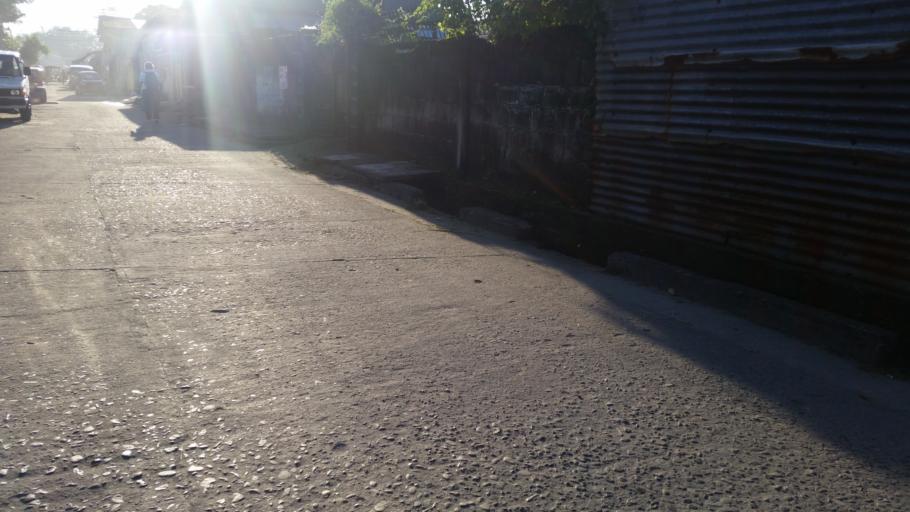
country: PH
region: Central Luzon
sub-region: Province of Pampanga
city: Mabalacat City
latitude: 15.2745
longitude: 120.5657
